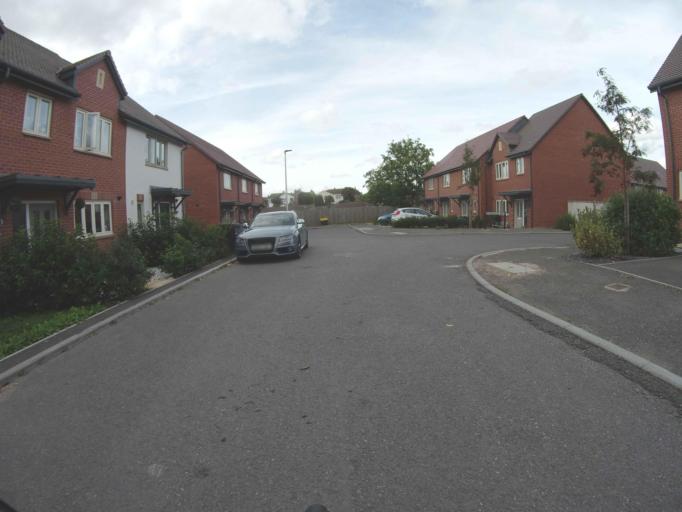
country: GB
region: England
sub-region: Devon
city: Exmouth
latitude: 50.6234
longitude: -3.3848
